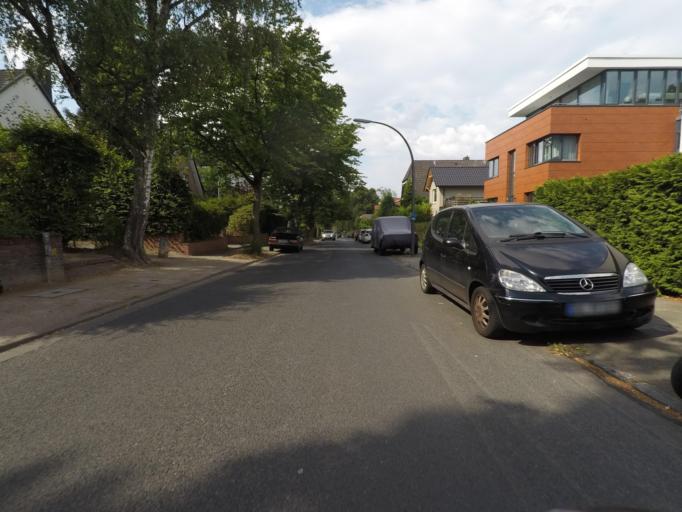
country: DE
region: Hamburg
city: Wellingsbuettel
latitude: 53.6373
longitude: 10.0643
